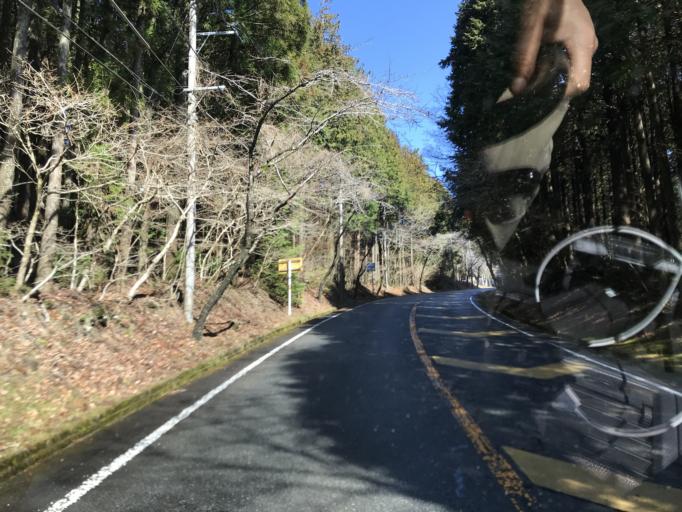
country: JP
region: Shizuoka
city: Fujinomiya
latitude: 35.2829
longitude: 138.6615
